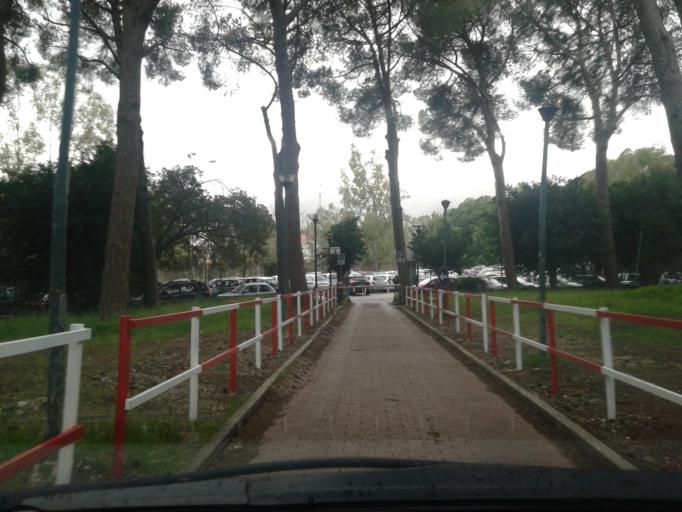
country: IT
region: Sicily
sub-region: Palermo
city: Monreale
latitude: 38.0933
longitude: 13.3114
